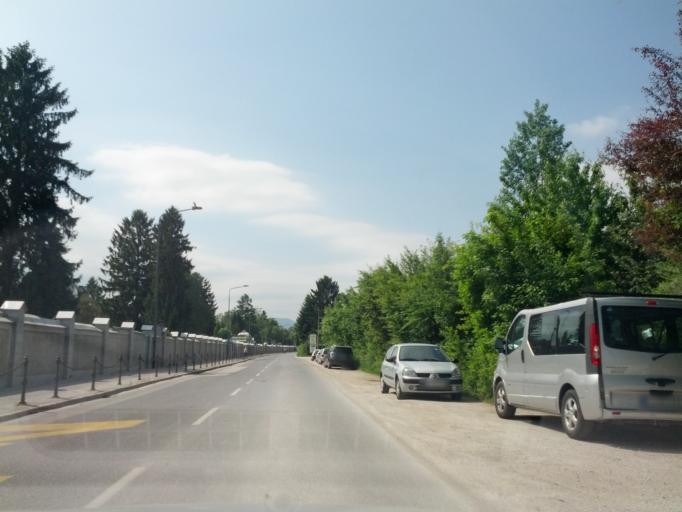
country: SI
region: Ljubljana
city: Ljubljana
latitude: 46.0717
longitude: 14.5296
